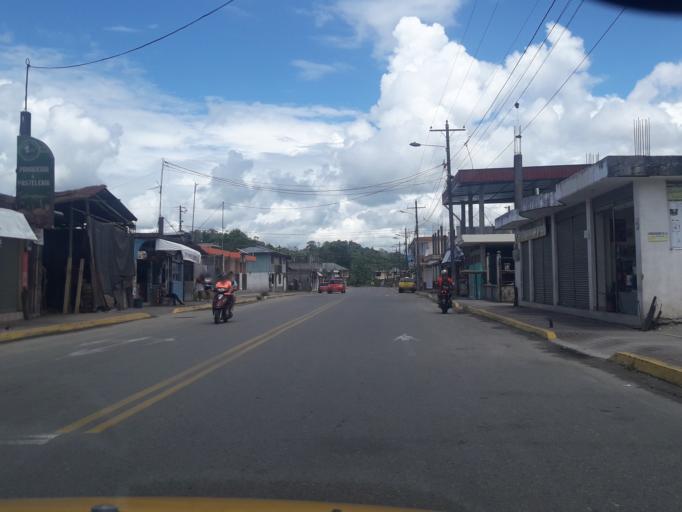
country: EC
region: Napo
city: Tena
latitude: -1.0053
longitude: -77.8190
